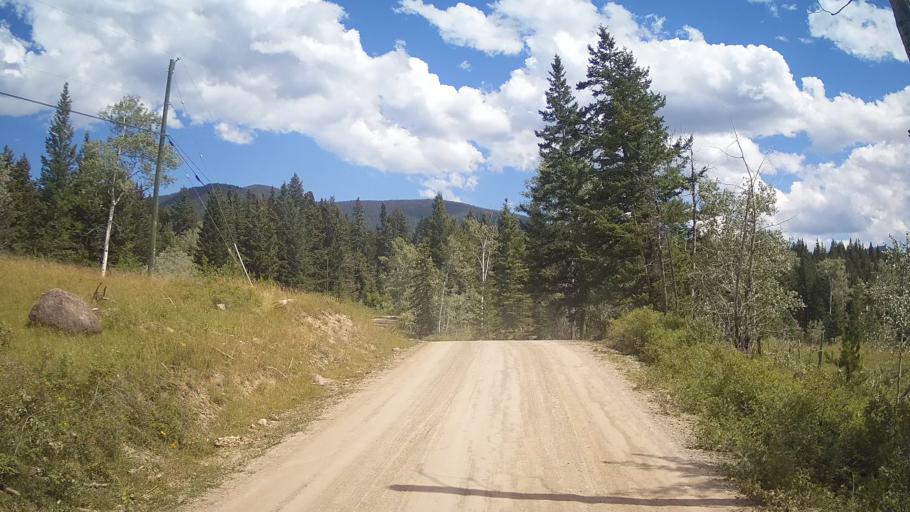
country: CA
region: British Columbia
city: Lillooet
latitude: 51.2874
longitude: -121.9721
